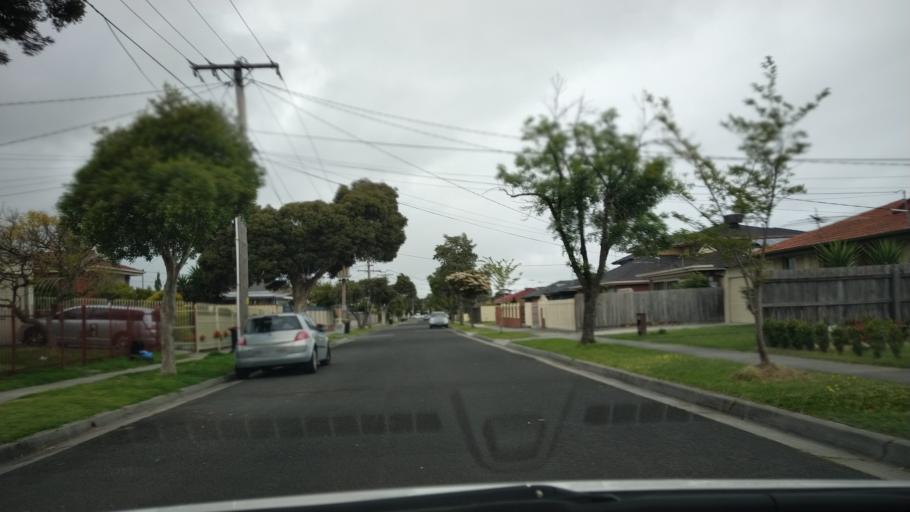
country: AU
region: Victoria
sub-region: Greater Dandenong
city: Keysborough
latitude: -37.9819
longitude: 145.1751
